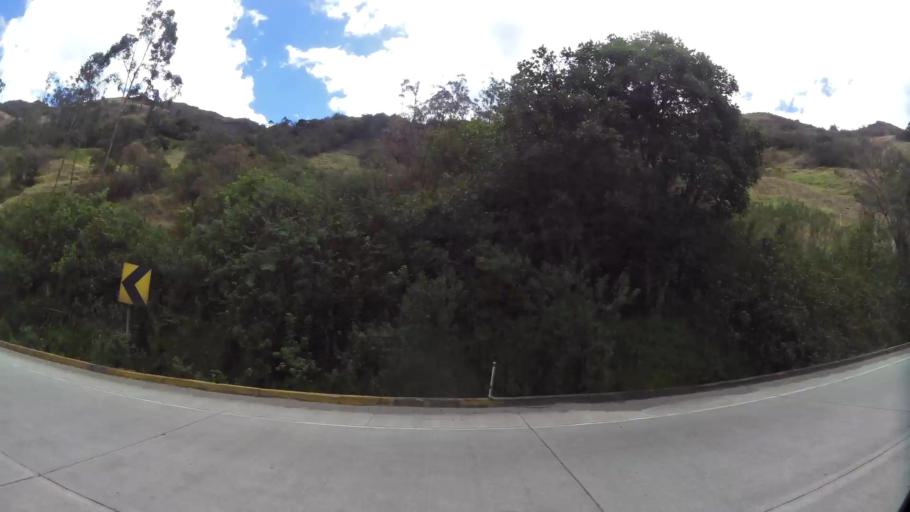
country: EC
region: Azuay
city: Cuenca
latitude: -3.1365
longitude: -79.1203
